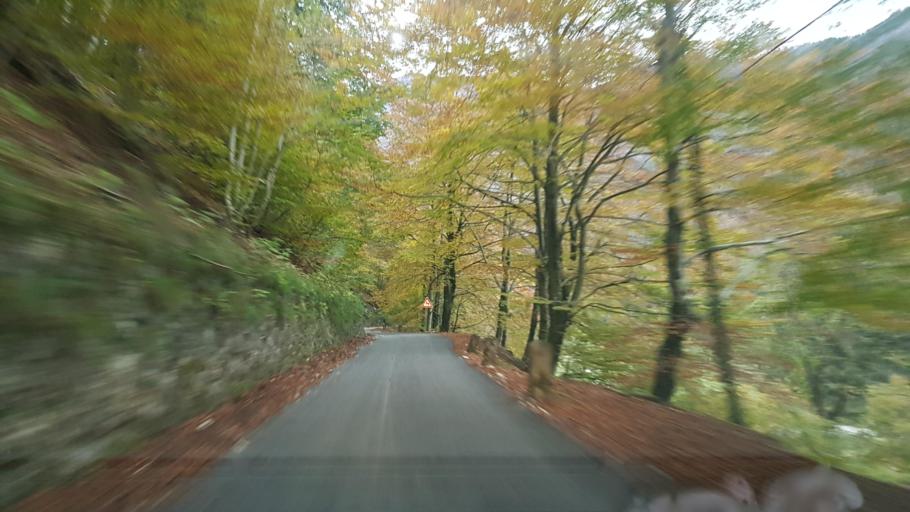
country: IT
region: Friuli Venezia Giulia
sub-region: Provincia di Udine
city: Preone
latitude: 46.3435
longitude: 12.8829
